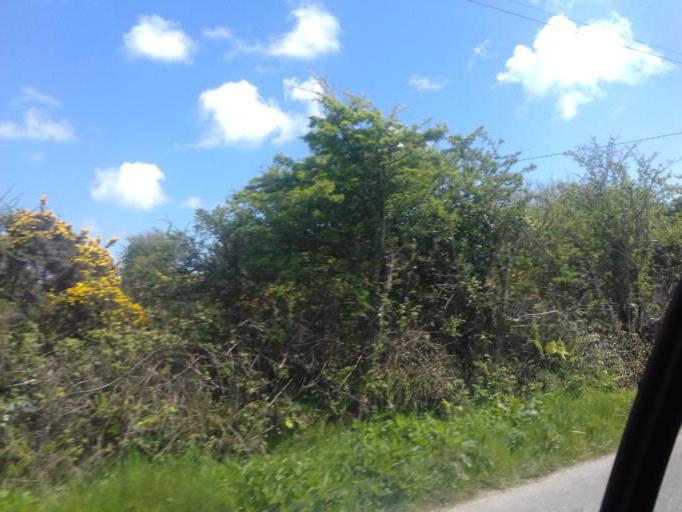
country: IE
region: Munster
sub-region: Waterford
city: Dunmore East
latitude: 52.2093
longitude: -6.8977
